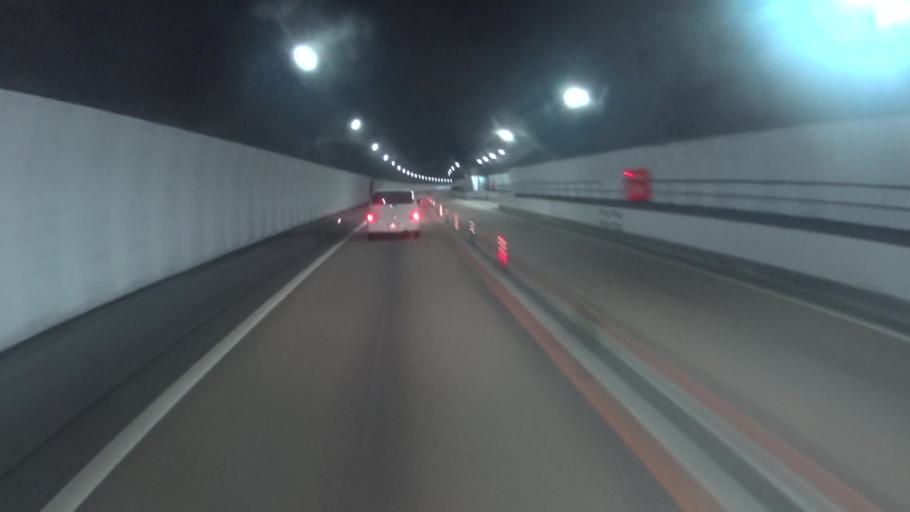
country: JP
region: Kyoto
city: Kameoka
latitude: 35.1377
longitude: 135.4518
